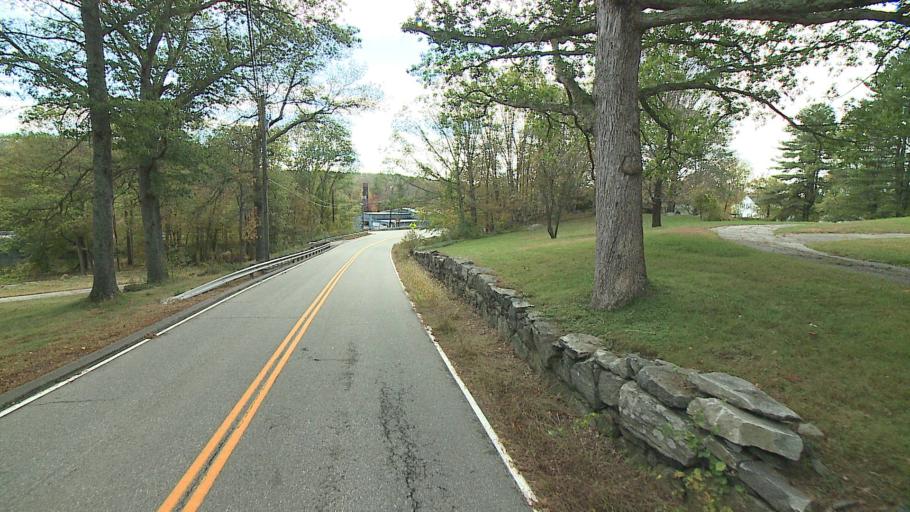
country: US
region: Connecticut
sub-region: Windham County
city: North Grosvenor Dale
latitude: 42.0141
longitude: -71.8877
